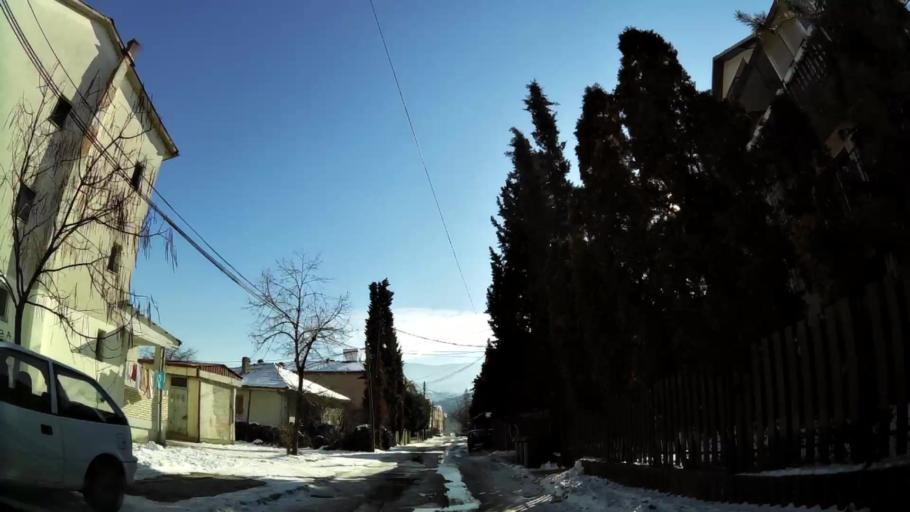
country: MK
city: Krushopek
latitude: 42.0050
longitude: 21.3602
